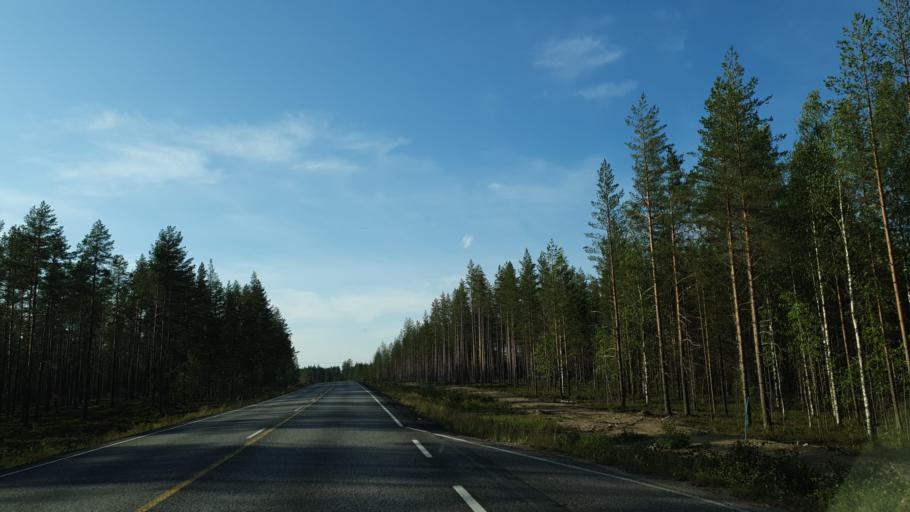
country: FI
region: Kainuu
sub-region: Kehys-Kainuu
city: Kuhmo
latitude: 64.0893
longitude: 29.4817
